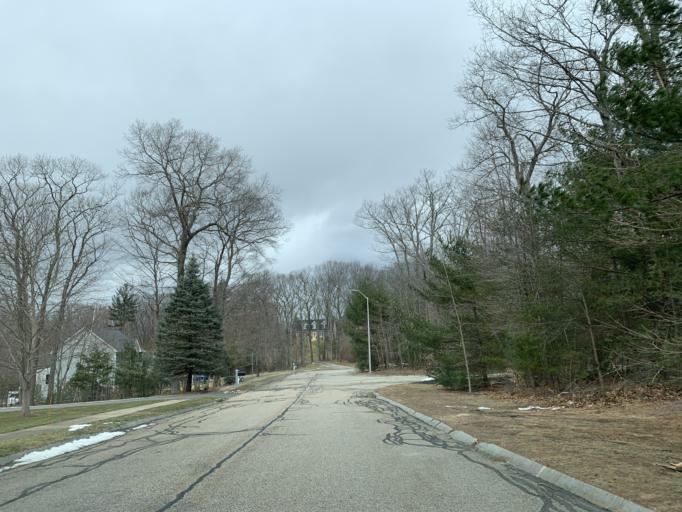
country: US
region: Massachusetts
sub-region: Norfolk County
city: Bellingham
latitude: 42.0453
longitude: -71.4538
